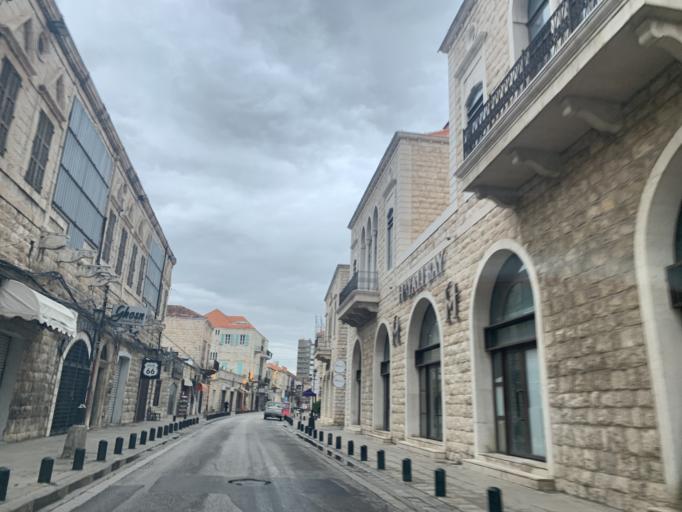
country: LB
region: Mont-Liban
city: Djounie
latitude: 33.9876
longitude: 35.6370
